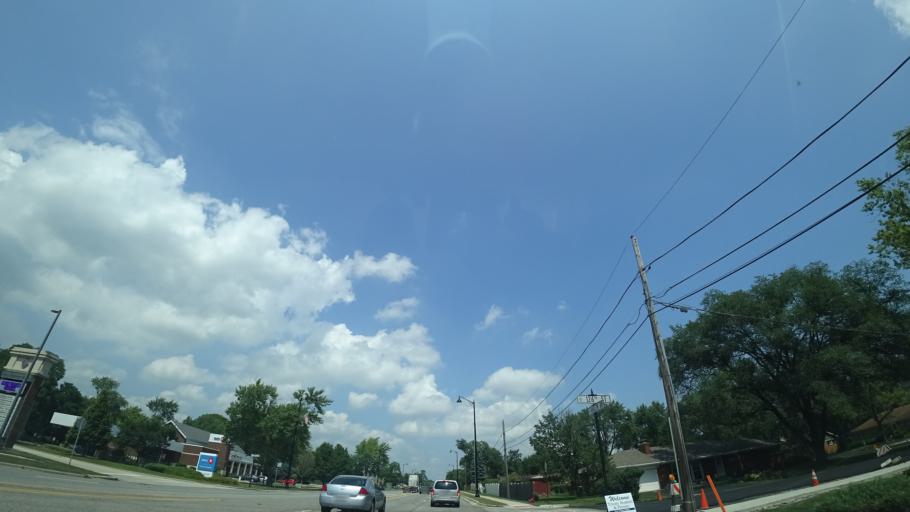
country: US
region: Illinois
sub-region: Cook County
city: Palos Heights
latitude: 41.6622
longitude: -87.7963
